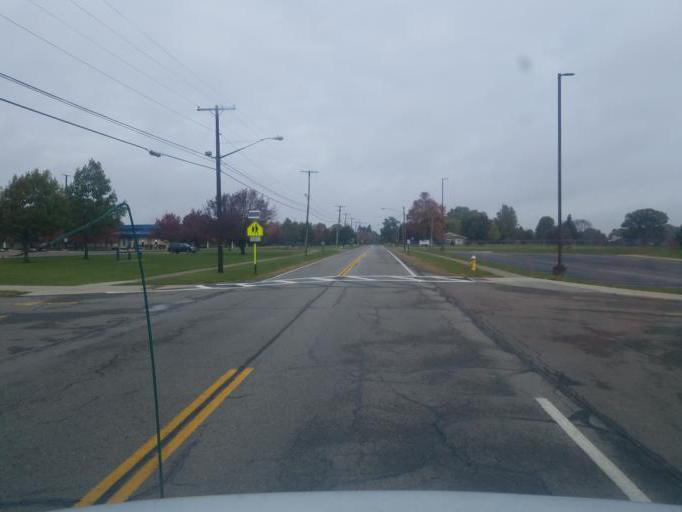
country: US
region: Ohio
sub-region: Richland County
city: Ontario
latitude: 40.7637
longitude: -82.6457
